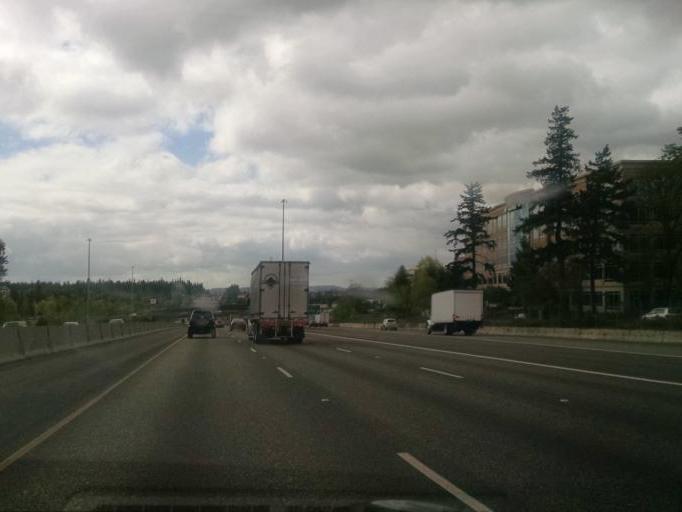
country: US
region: Oregon
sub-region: Washington County
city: Durham
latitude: 45.4254
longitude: -122.7442
